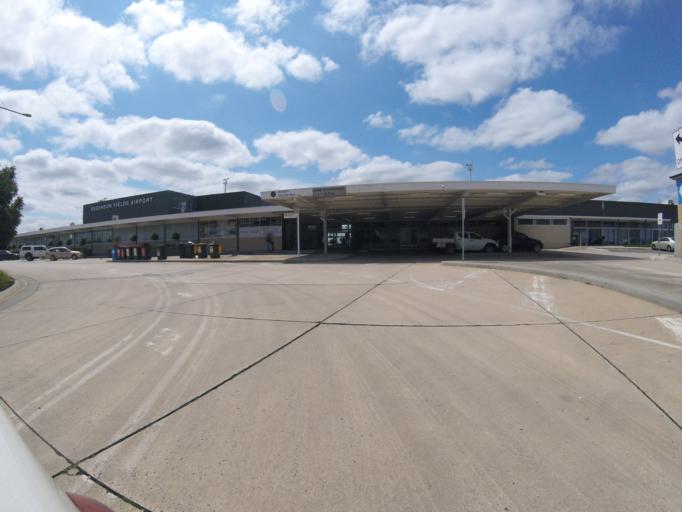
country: AU
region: Victoria
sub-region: Moonee Valley
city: Niddrie
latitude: -37.7278
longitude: 144.8970
